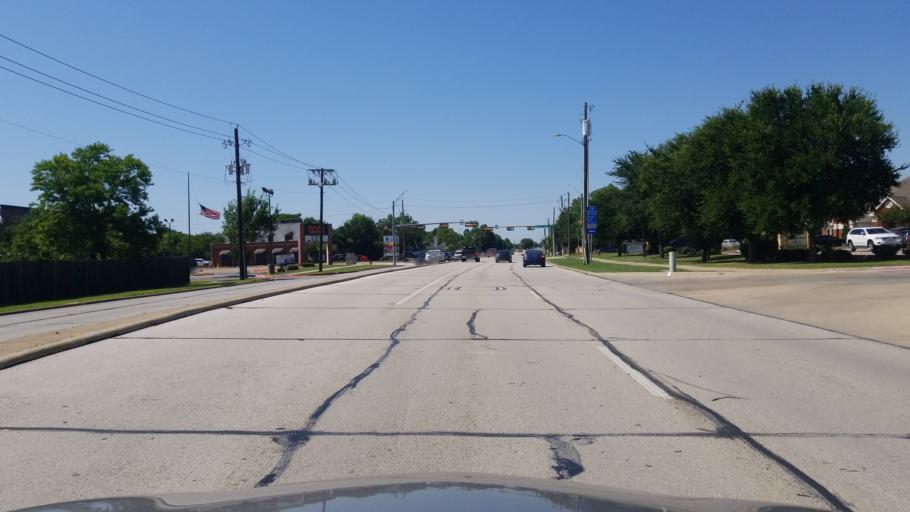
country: US
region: Texas
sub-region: Dallas County
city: Grand Prairie
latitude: 32.6910
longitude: -97.0155
